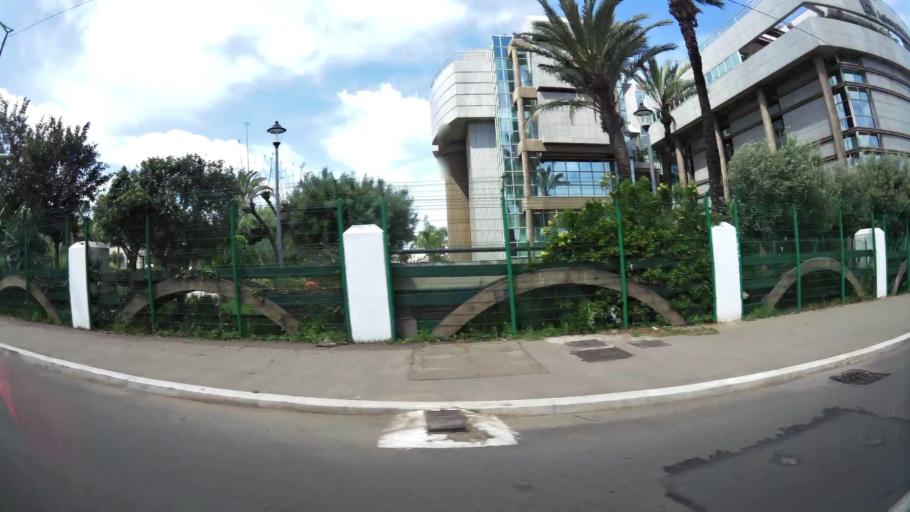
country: MA
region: Grand Casablanca
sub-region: Casablanca
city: Casablanca
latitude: 33.5506
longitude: -7.6323
